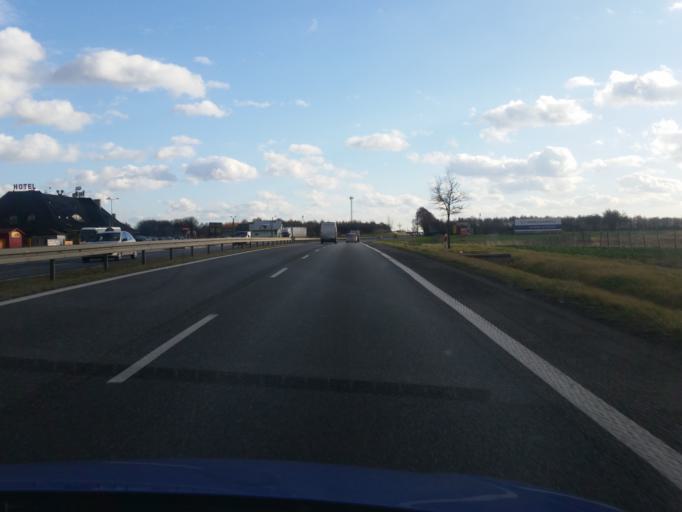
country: PL
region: Silesian Voivodeship
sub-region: Powiat myszkowski
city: Kozieglowy
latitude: 50.6154
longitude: 19.1507
